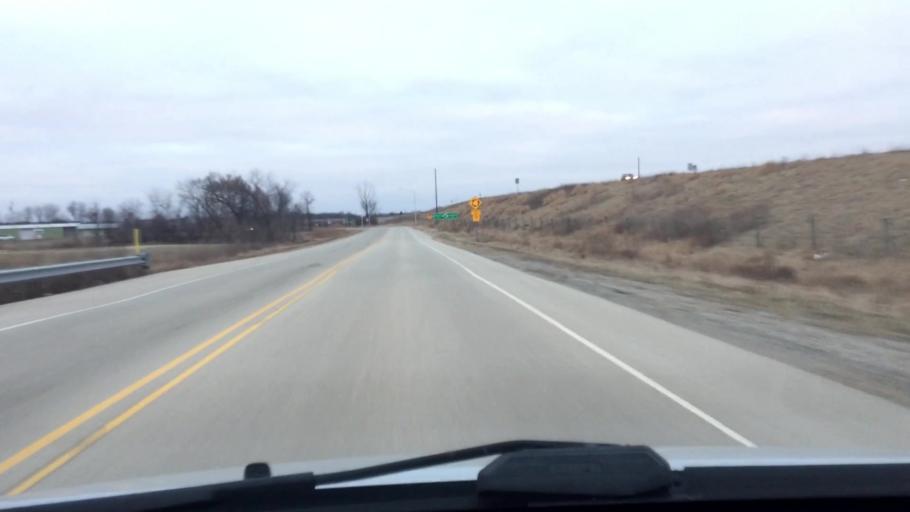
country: US
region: Wisconsin
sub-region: Jefferson County
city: Watertown
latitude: 43.1594
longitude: -88.7521
